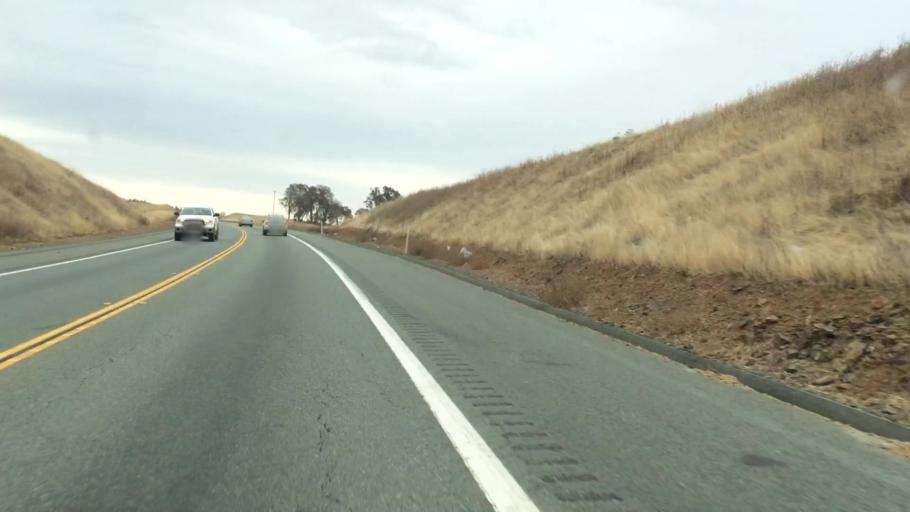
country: US
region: California
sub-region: Amador County
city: Sutter Creek
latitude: 38.3882
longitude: -120.8143
